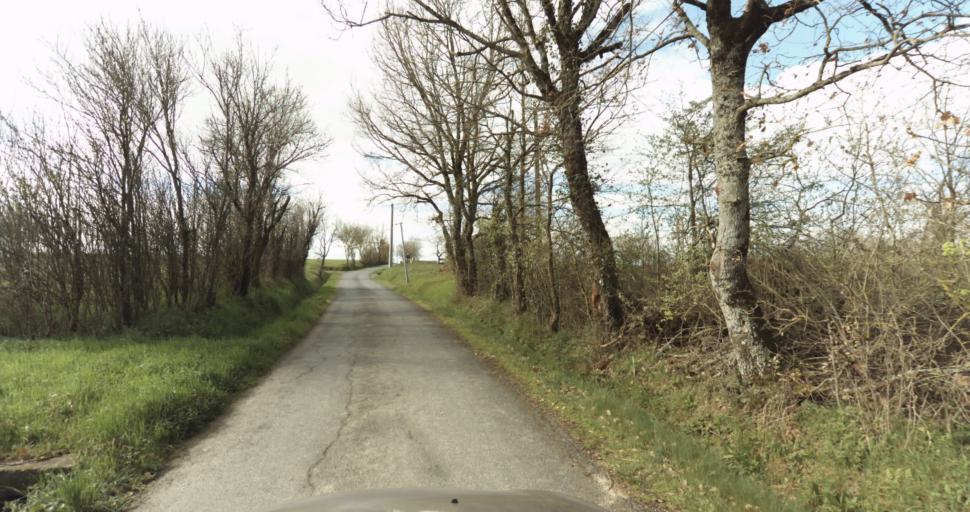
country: FR
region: Midi-Pyrenees
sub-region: Departement du Tarn
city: Frejairolles
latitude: 43.8584
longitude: 2.2079
